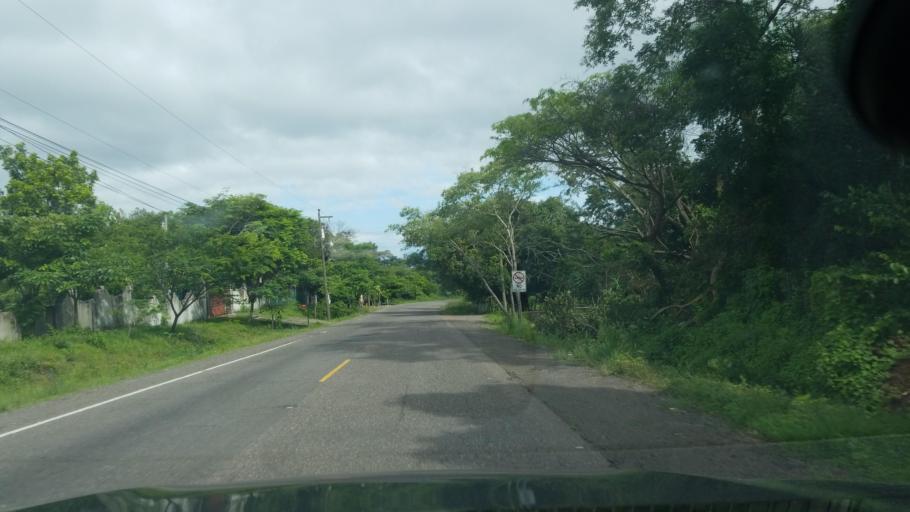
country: HN
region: Choluteca
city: Corpus
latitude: 13.3681
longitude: -86.9574
